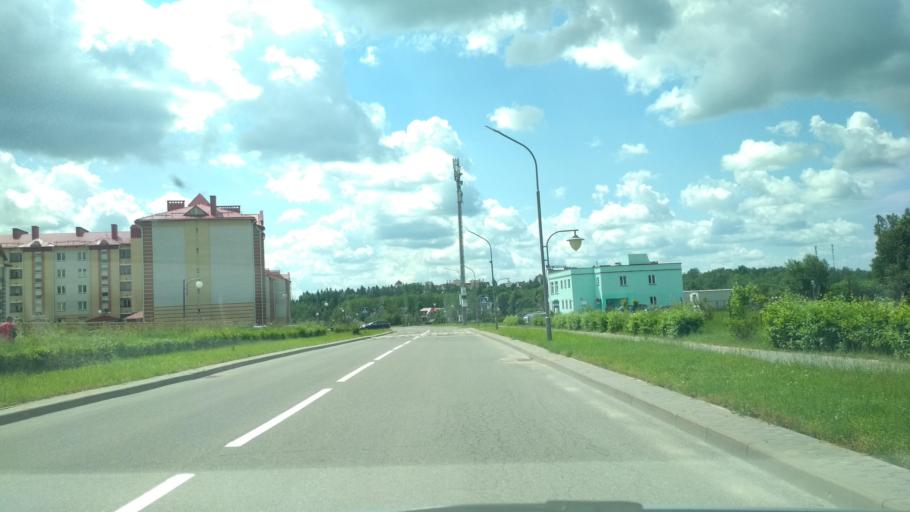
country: BY
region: Grodnenskaya
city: Astravyets
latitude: 54.6163
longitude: 25.9764
